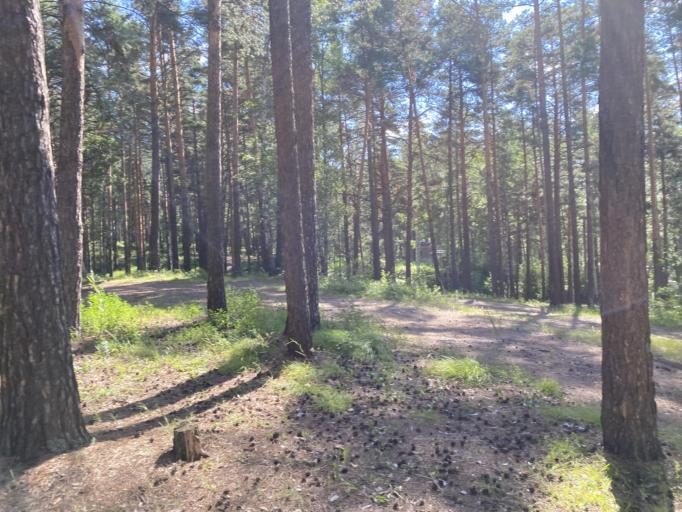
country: RU
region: Novosibirsk
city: Akademgorodok
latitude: 54.8342
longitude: 83.0721
